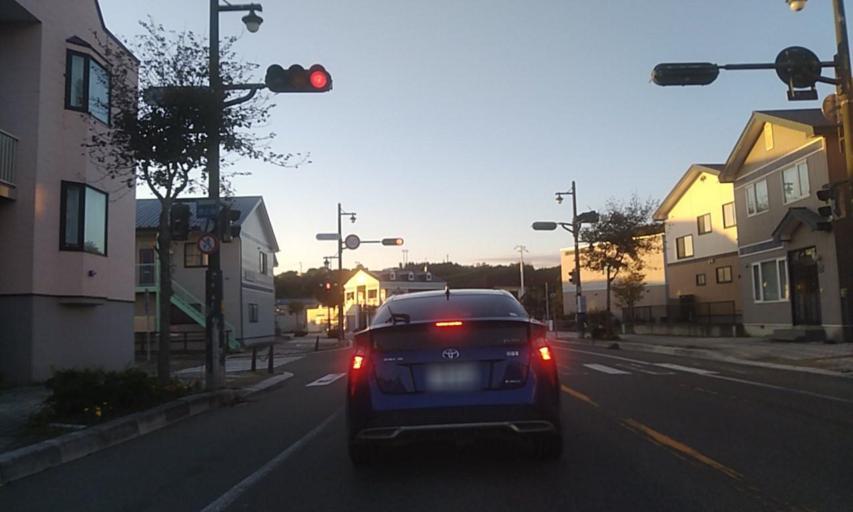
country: JP
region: Hokkaido
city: Shizunai-furukawacho
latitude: 42.1596
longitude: 142.7814
